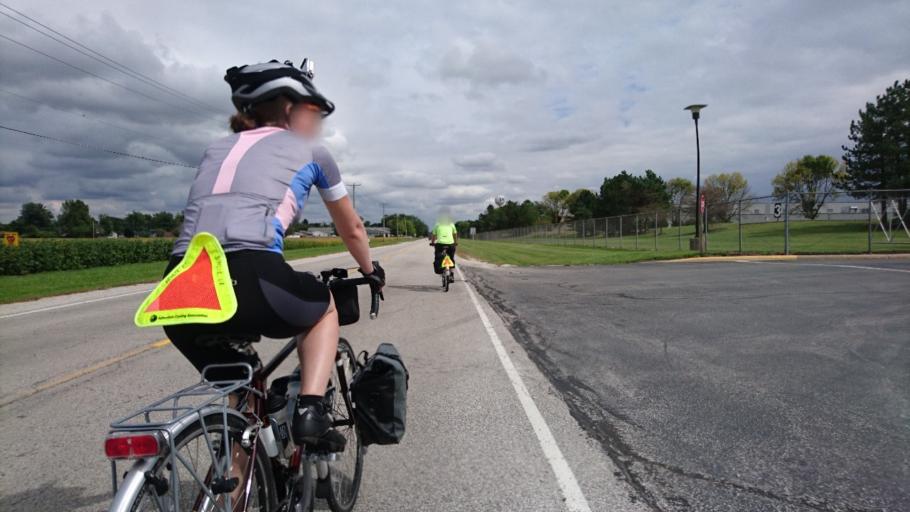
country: US
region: Illinois
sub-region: Livingston County
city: Pontiac
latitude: 40.8880
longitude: -88.6573
